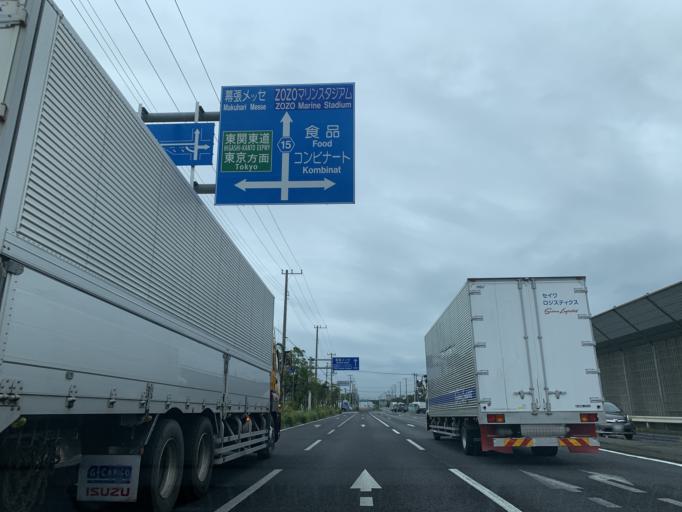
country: JP
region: Chiba
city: Funabashi
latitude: 35.6767
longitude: 139.9992
